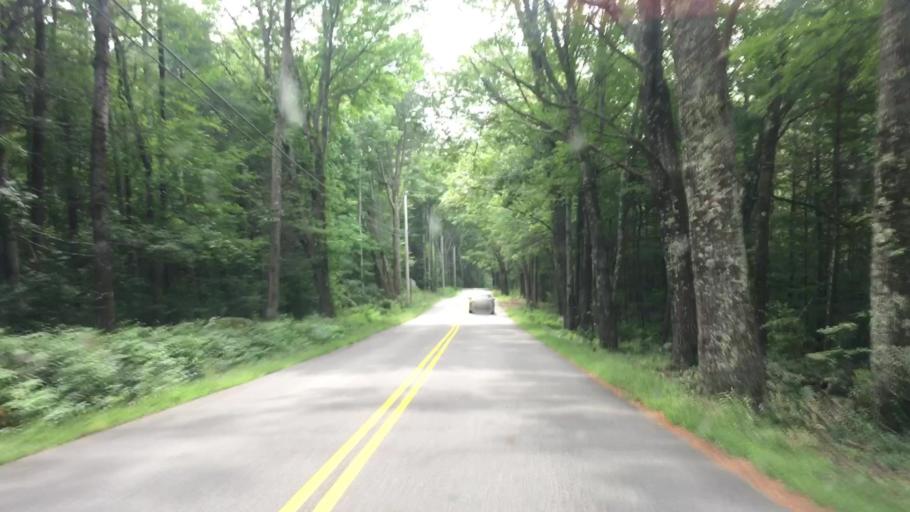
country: US
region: New Hampshire
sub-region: Strafford County
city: Madbury
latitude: 43.2059
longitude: -70.9751
